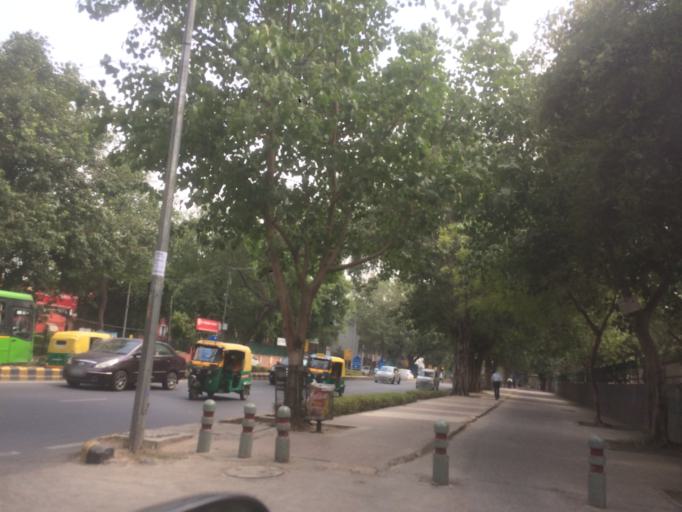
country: IN
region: NCT
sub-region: Central Delhi
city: Karol Bagh
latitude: 28.6389
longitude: 77.2038
